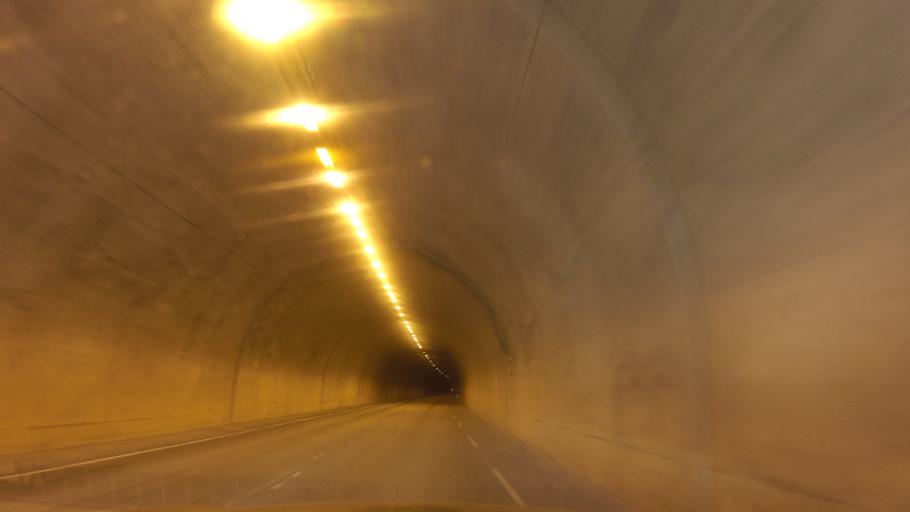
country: IS
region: Westfjords
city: Isafjoerdur
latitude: 66.1431
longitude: -23.2230
